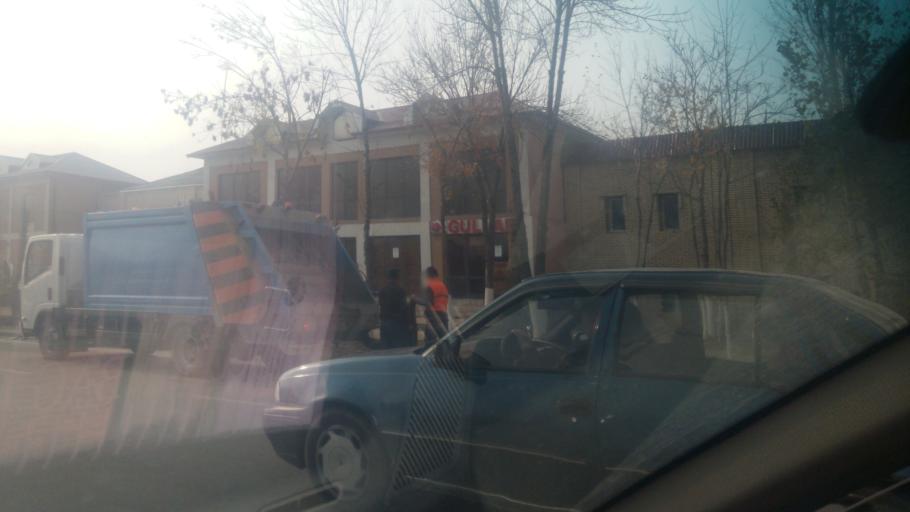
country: UZ
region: Sirdaryo
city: Guliston
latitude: 40.5003
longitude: 68.7739
